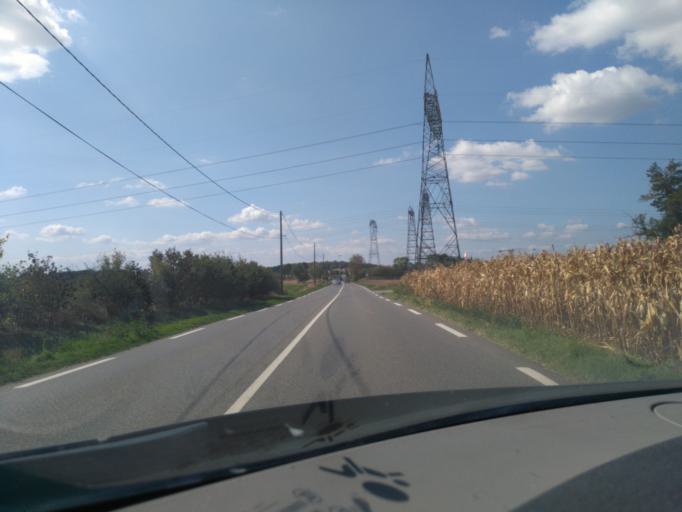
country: FR
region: Rhone-Alpes
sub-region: Departement du Rhone
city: Saint-Bonnet-de-Mure
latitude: 45.7259
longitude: 5.0332
